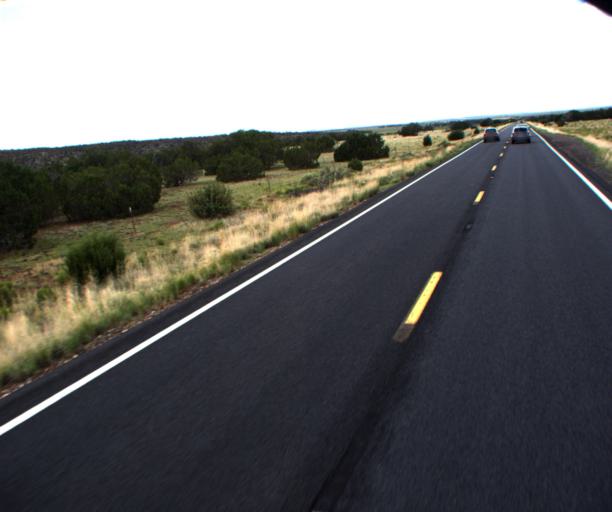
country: US
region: Arizona
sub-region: Coconino County
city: Parks
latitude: 35.5800
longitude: -111.9519
